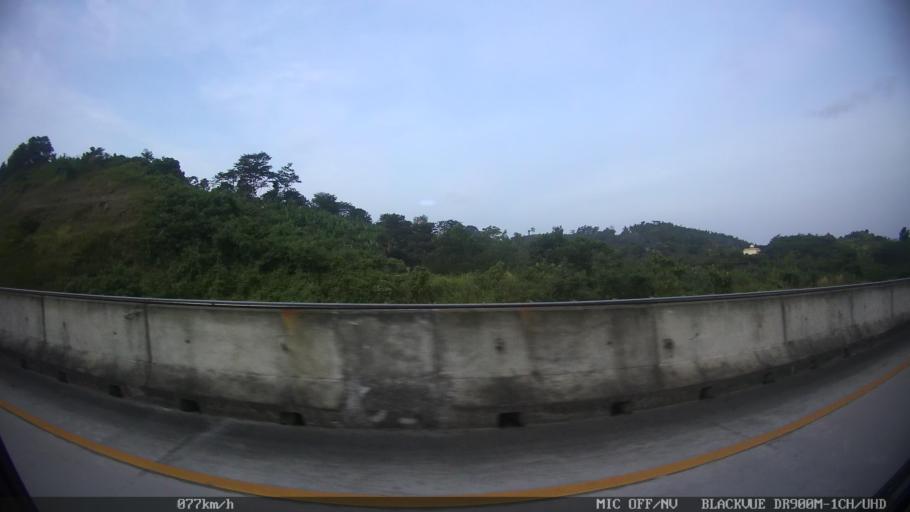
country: ID
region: Lampung
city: Penengahan
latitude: -5.8580
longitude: 105.7313
